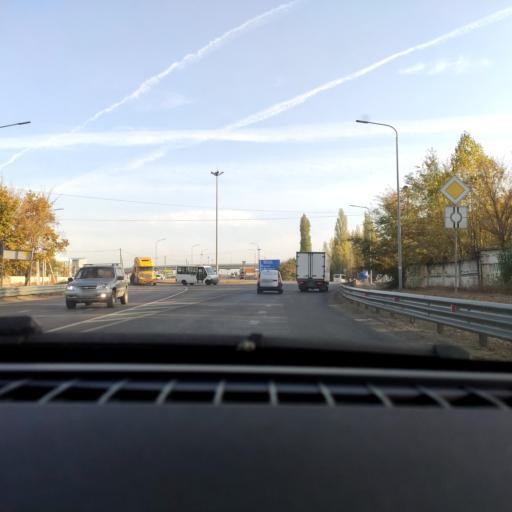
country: RU
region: Voronezj
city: Maslovka
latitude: 51.6454
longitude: 39.2973
